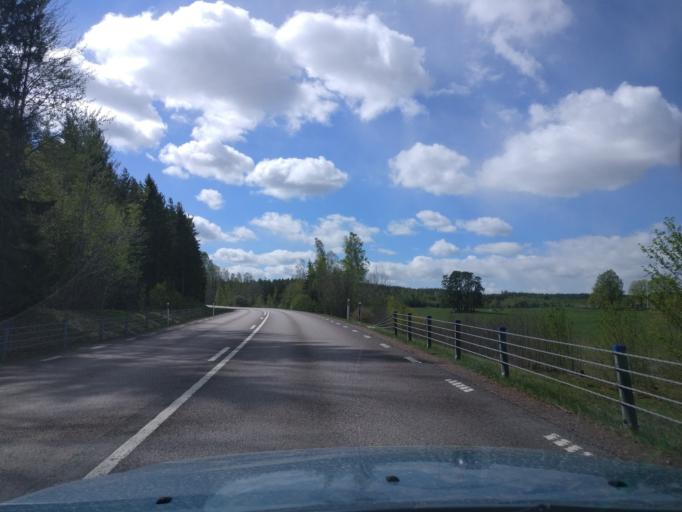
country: SE
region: Vaermland
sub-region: Karlstads Kommun
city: Molkom
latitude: 59.5413
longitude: 13.6232
